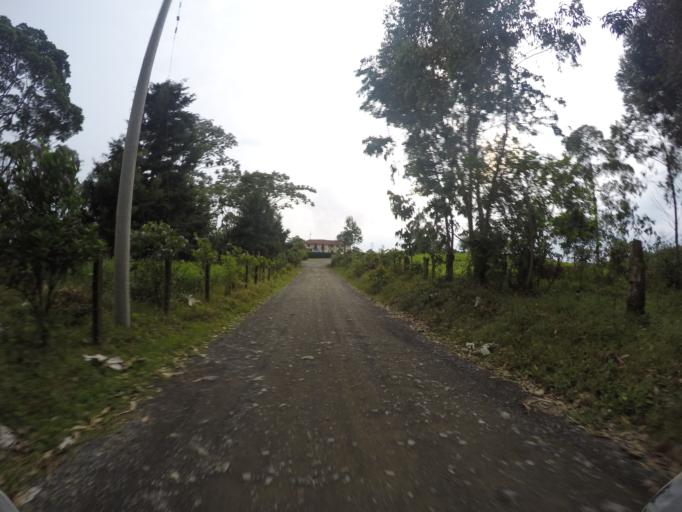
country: CO
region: Quindio
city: Filandia
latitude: 4.7126
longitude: -75.6315
